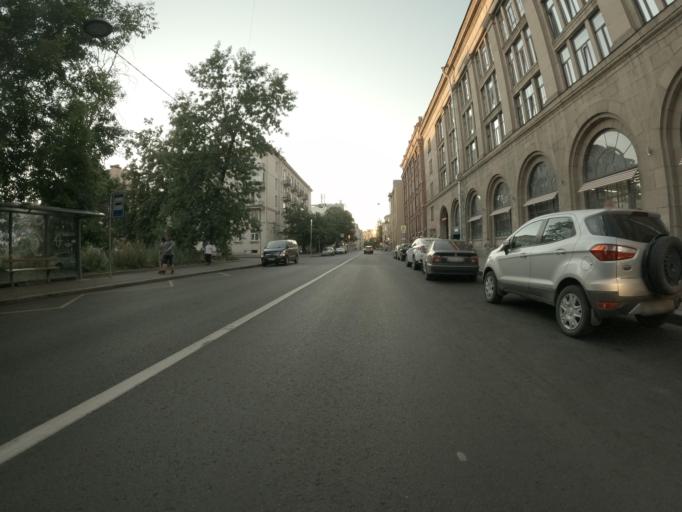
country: RU
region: St.-Petersburg
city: Petrogradka
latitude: 59.9579
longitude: 30.3130
